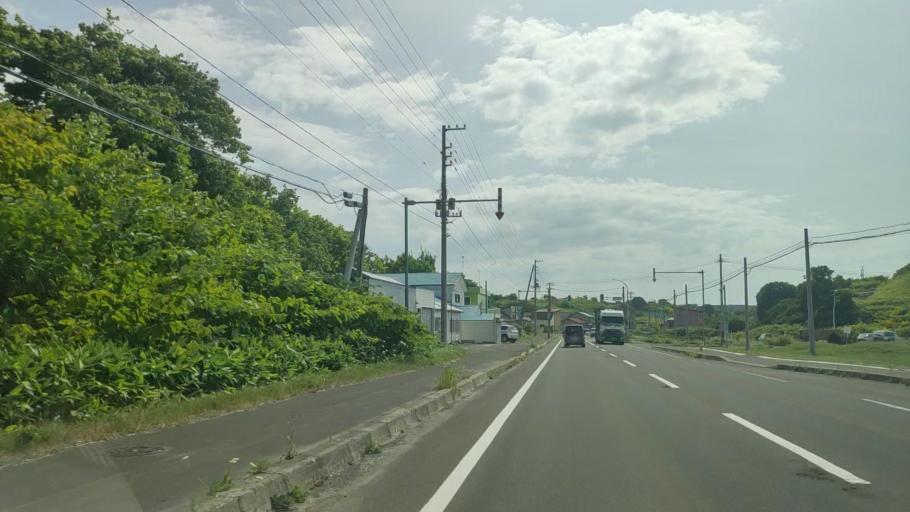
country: JP
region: Hokkaido
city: Rumoi
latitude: 44.3154
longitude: 141.6631
